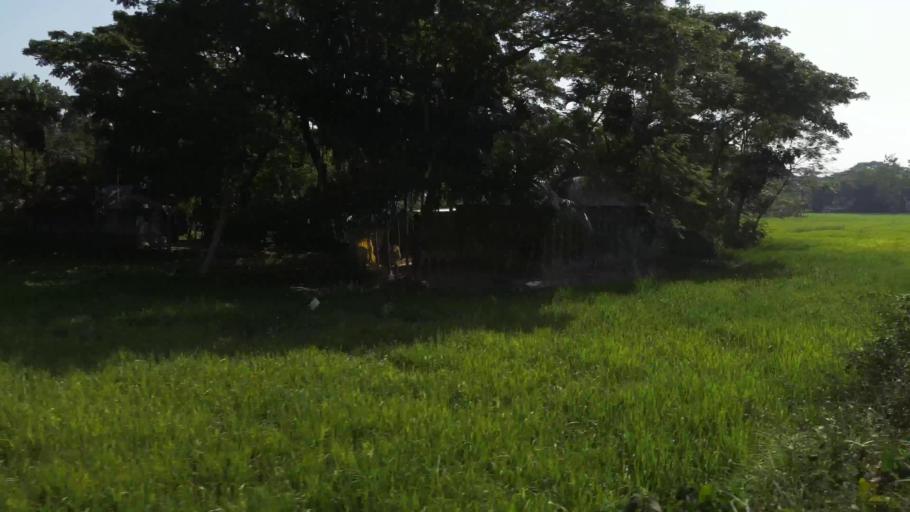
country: BD
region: Dhaka
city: Gafargaon
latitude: 24.5915
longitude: 90.5033
